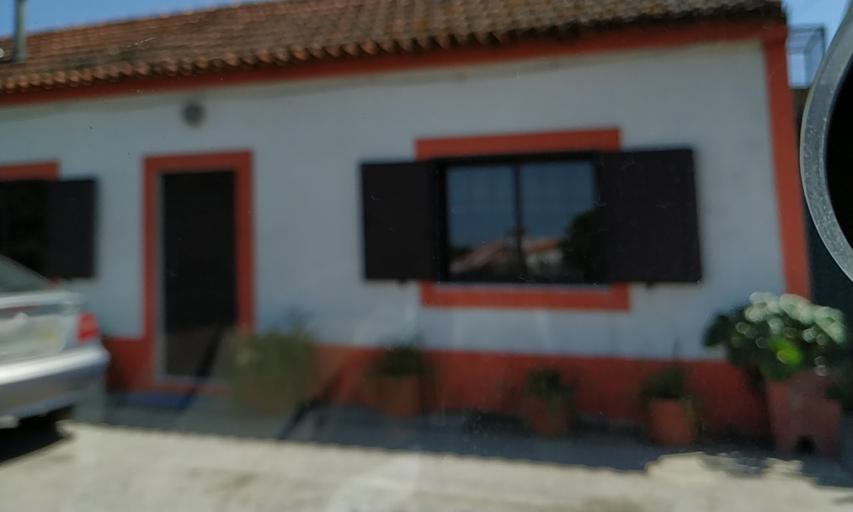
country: PT
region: Setubal
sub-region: Palmela
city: Palmela
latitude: 38.6145
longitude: -8.7603
